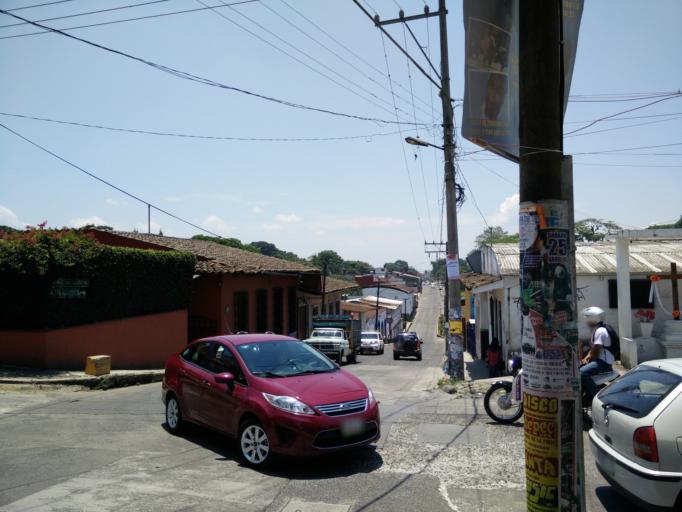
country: MX
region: Veracruz
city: Coatepec
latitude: 19.4521
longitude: -96.9529
